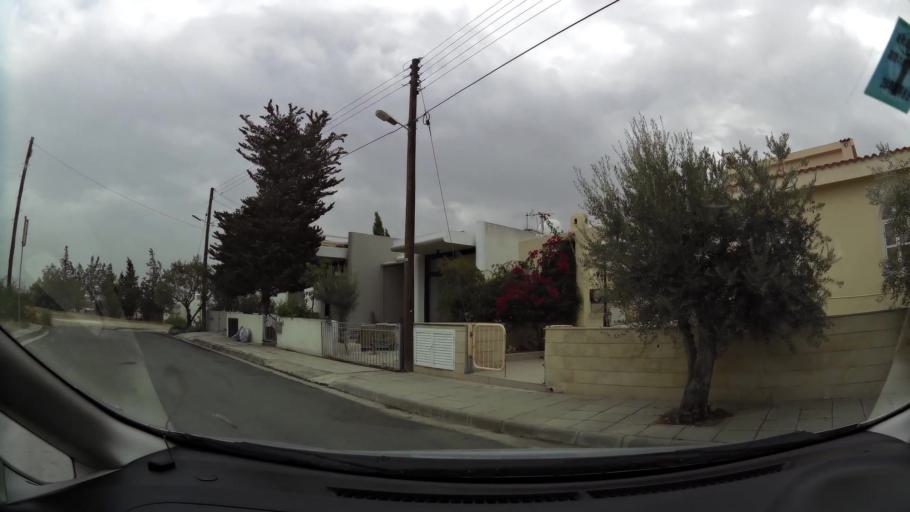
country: CY
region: Lefkosia
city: Geri
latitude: 35.1094
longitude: 33.3810
